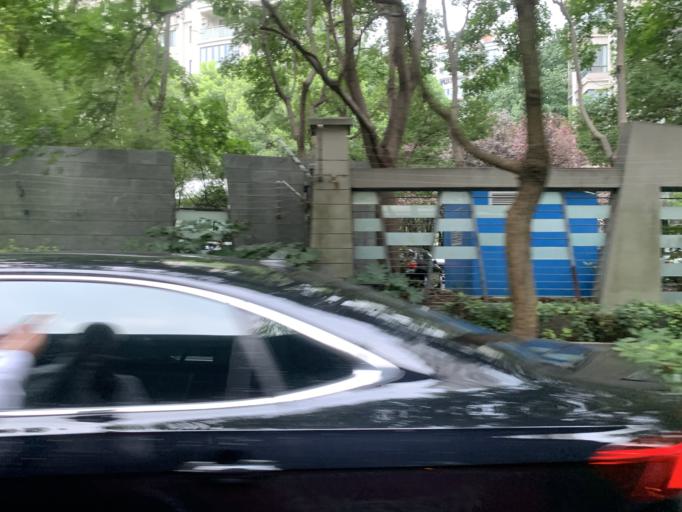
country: CN
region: Shanghai Shi
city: Huamu
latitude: 31.2297
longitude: 121.5601
